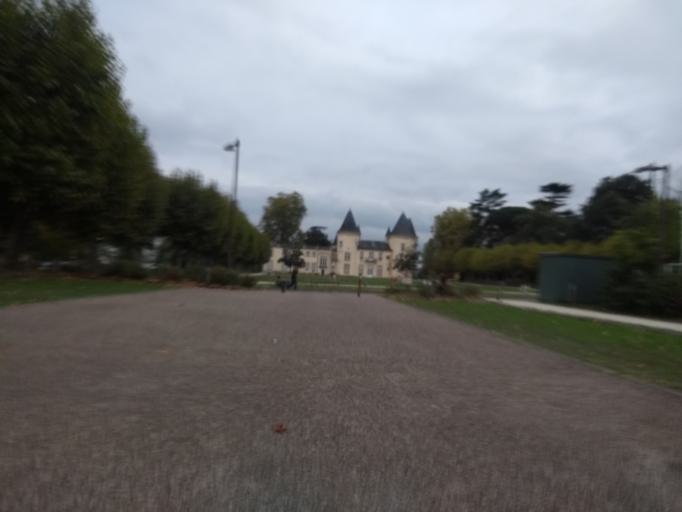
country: FR
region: Aquitaine
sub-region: Departement de la Gironde
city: Talence
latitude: 44.7903
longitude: -0.5916
